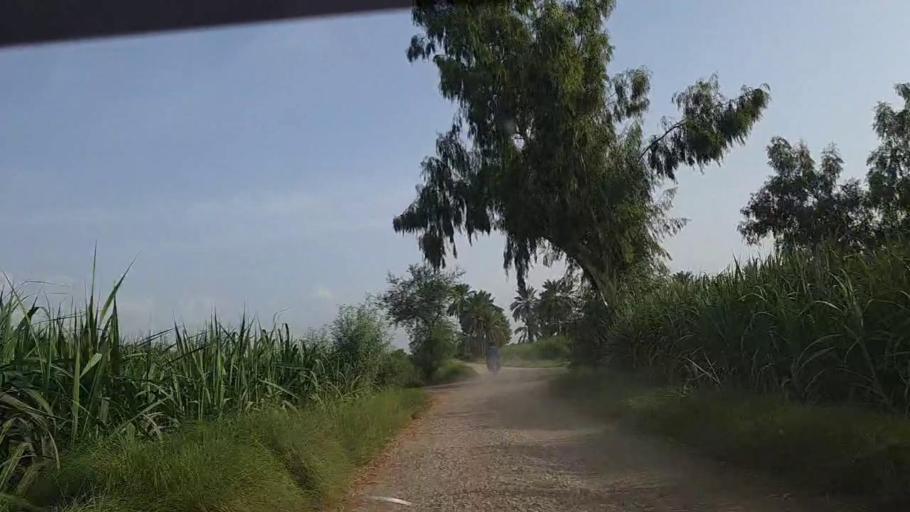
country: PK
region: Sindh
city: Ghotki
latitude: 27.9746
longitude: 69.2559
